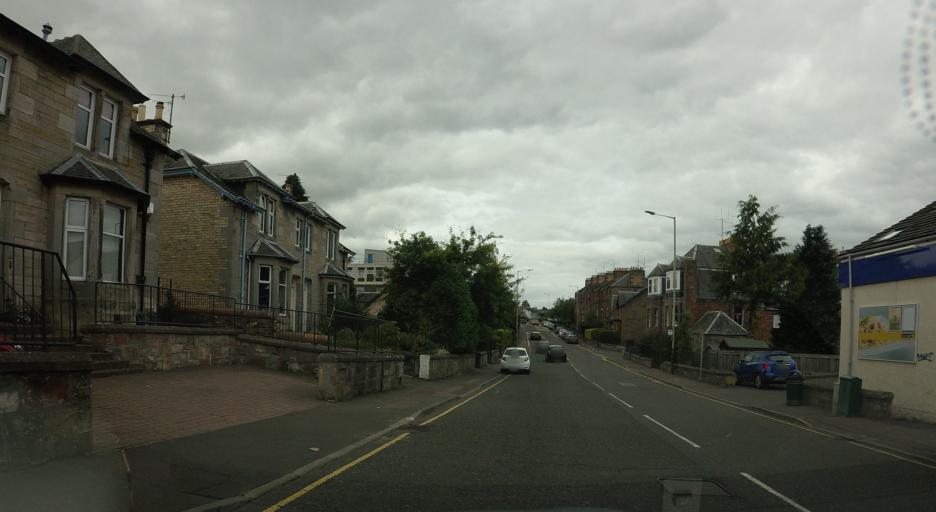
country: GB
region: Scotland
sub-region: Perth and Kinross
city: Perth
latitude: 56.3981
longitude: -3.4526
